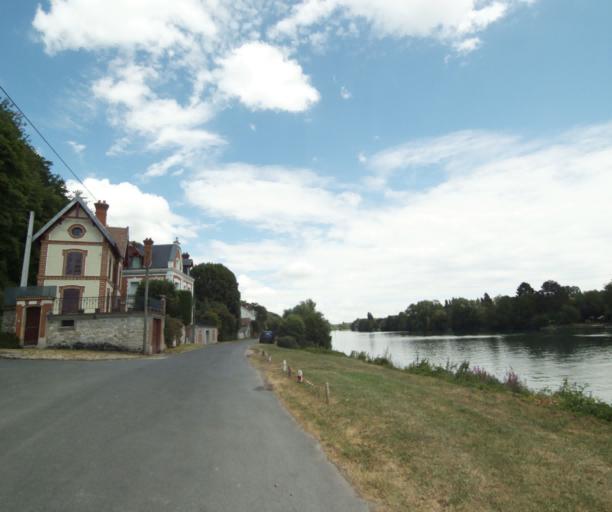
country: FR
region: Ile-de-France
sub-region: Departement de Seine-et-Marne
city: Samoreau
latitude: 48.4359
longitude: 2.7446
